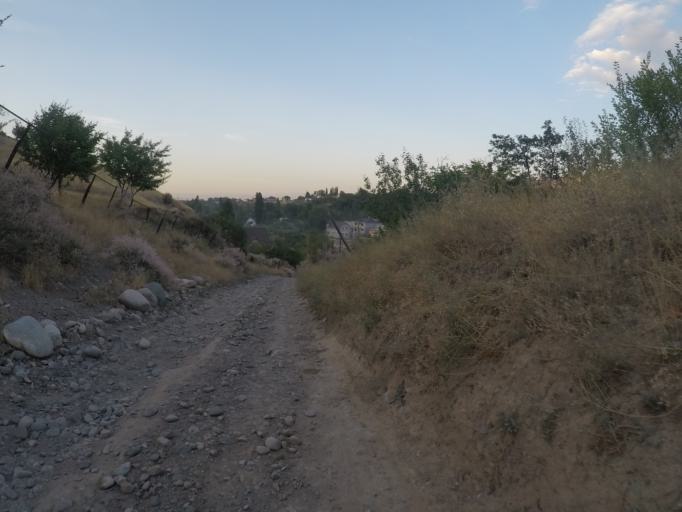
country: KG
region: Chuy
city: Bishkek
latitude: 42.7734
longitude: 74.6404
